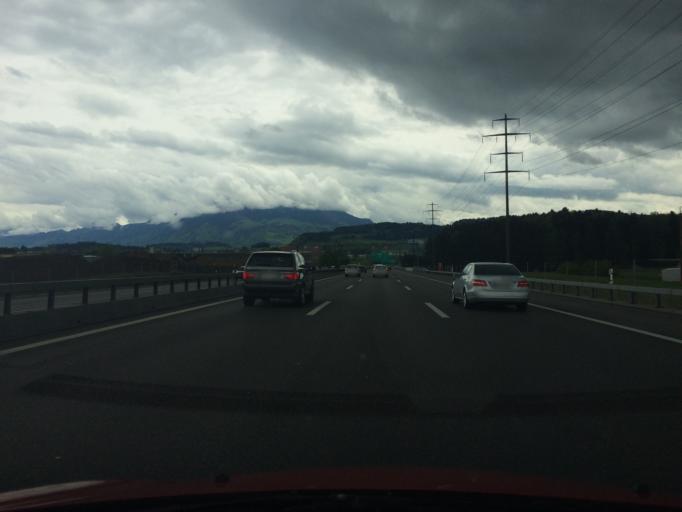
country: CH
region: Zug
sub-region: Zug
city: Hunenberg
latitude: 47.1655
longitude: 8.4325
